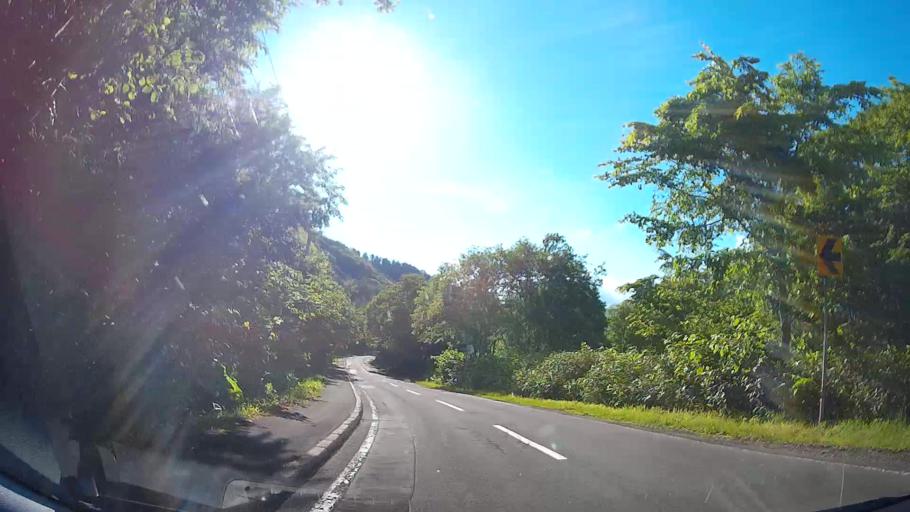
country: JP
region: Hokkaido
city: Sapporo
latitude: 42.9750
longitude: 141.1423
